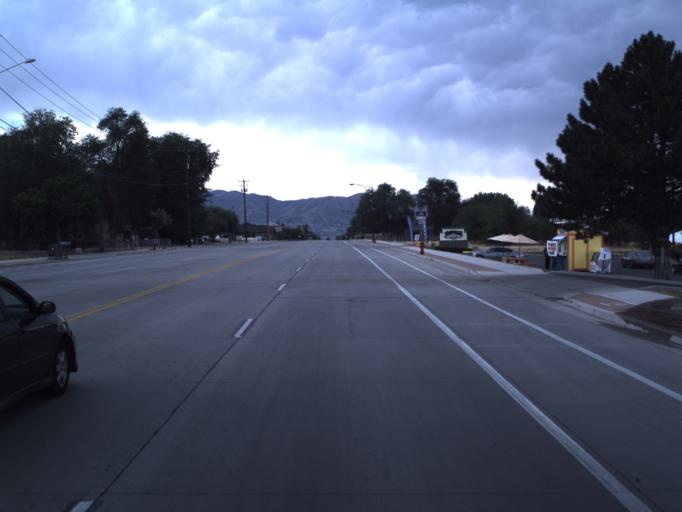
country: US
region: Utah
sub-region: Salt Lake County
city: White City
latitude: 40.5580
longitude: -111.8723
